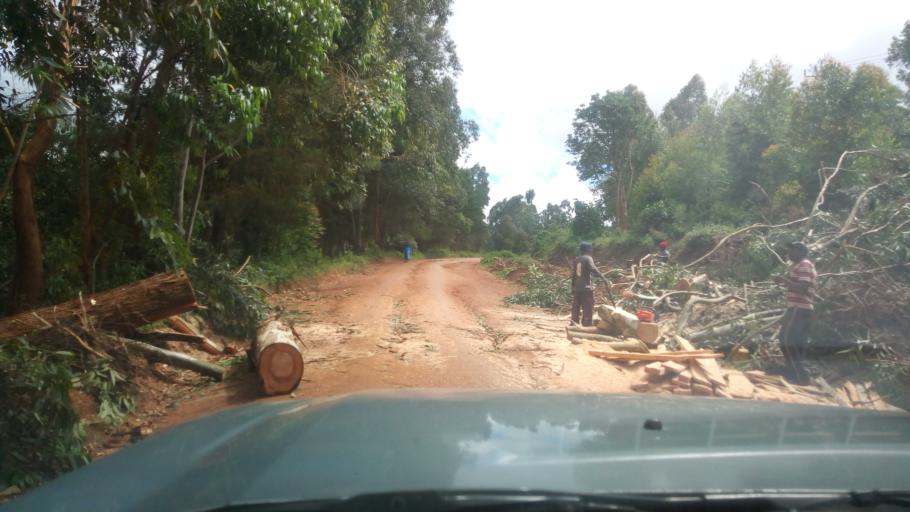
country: KE
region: Makueni
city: Wote
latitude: -1.6693
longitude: 37.4495
